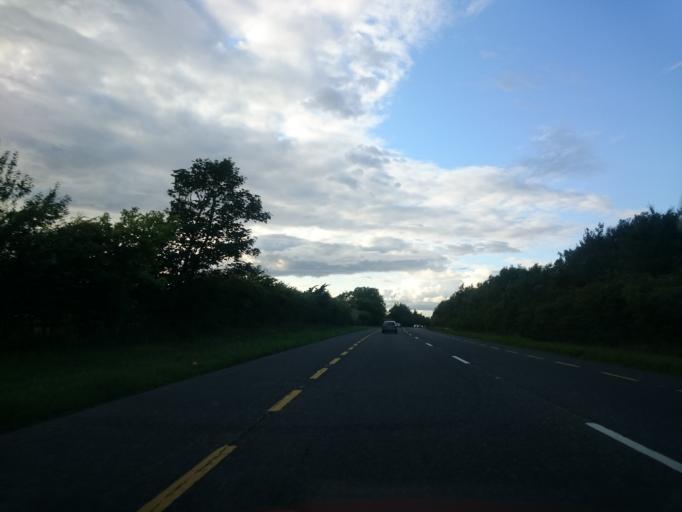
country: IE
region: Leinster
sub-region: Loch Garman
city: Castlebridge
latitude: 52.3884
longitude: -6.5187
